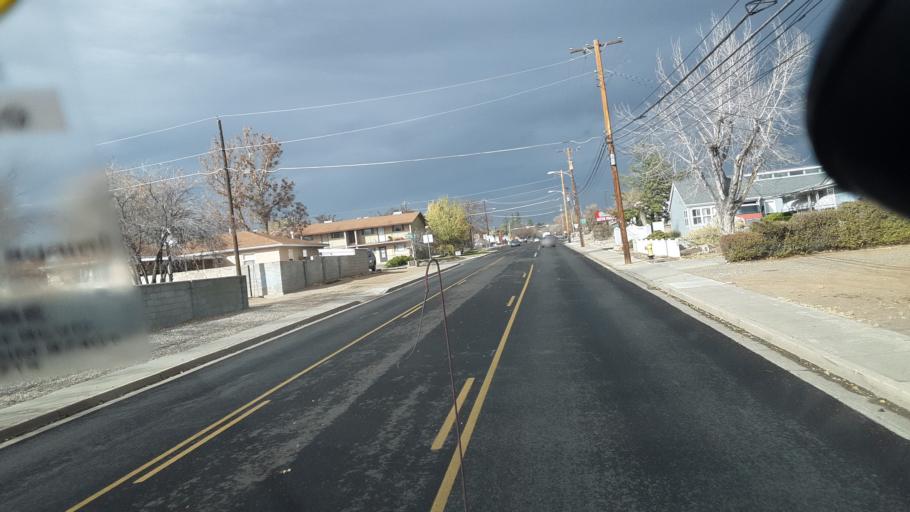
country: US
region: New Mexico
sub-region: San Juan County
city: Farmington
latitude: 36.7457
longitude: -108.1977
